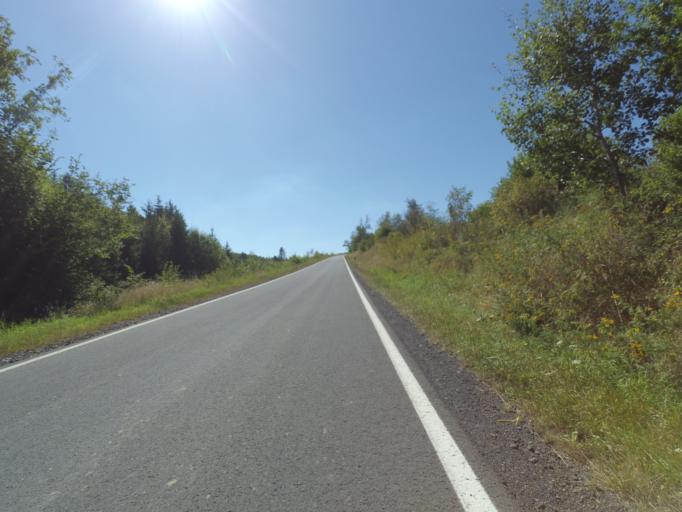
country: DE
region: Rheinland-Pfalz
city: Demerath
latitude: 50.1978
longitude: 6.9514
